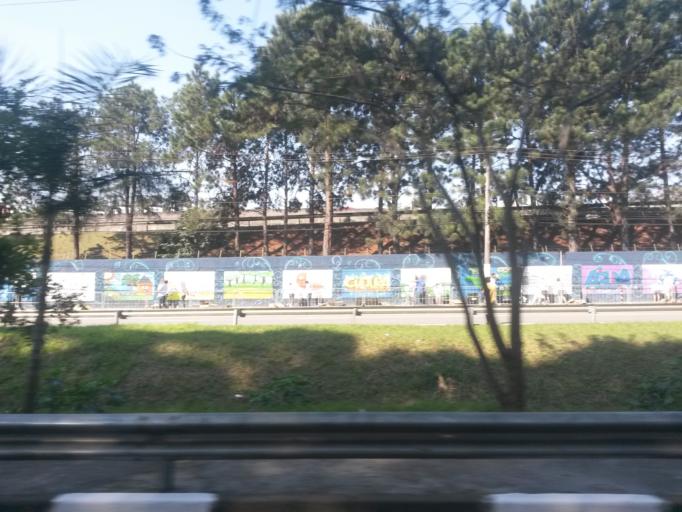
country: BR
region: Sao Paulo
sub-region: Sao Bernardo Do Campo
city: Sao Bernardo do Campo
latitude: -23.7137
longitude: -46.5738
